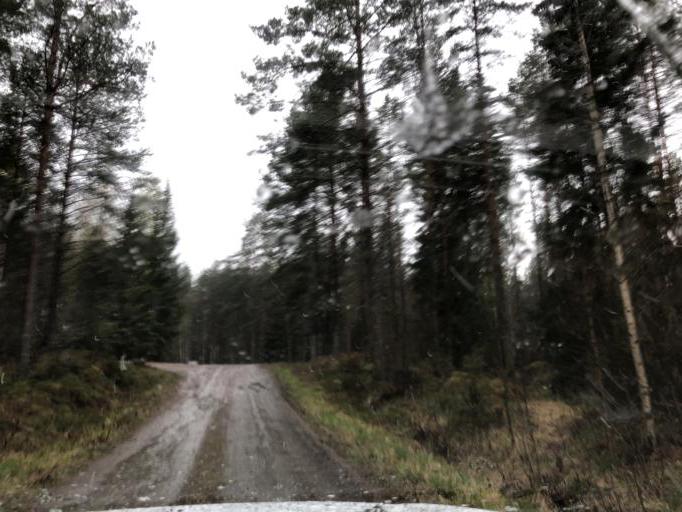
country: SE
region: Uppsala
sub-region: Heby Kommun
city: Tarnsjo
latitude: 60.2082
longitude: 16.8925
